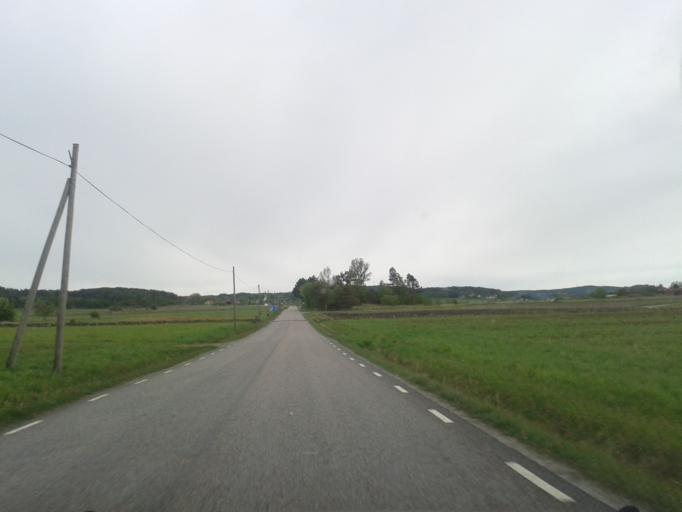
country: SE
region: Vaestra Goetaland
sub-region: Kungalvs Kommun
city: Kode
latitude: 57.9584
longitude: 11.8219
